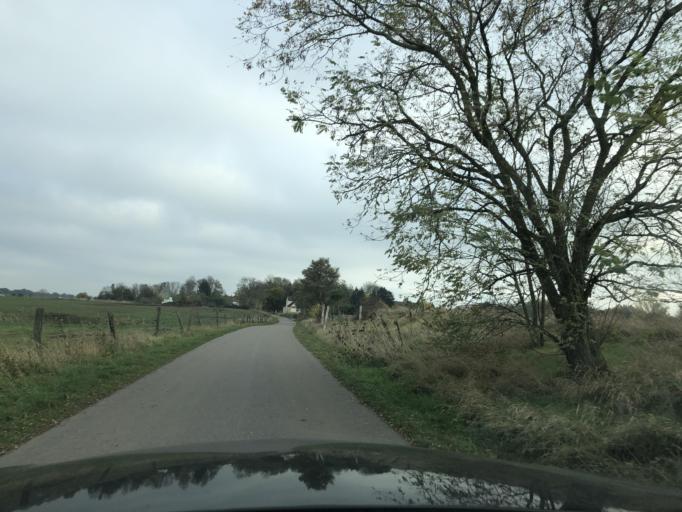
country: DE
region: Mecklenburg-Vorpommern
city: Kessin
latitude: 53.7468
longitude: 13.3430
